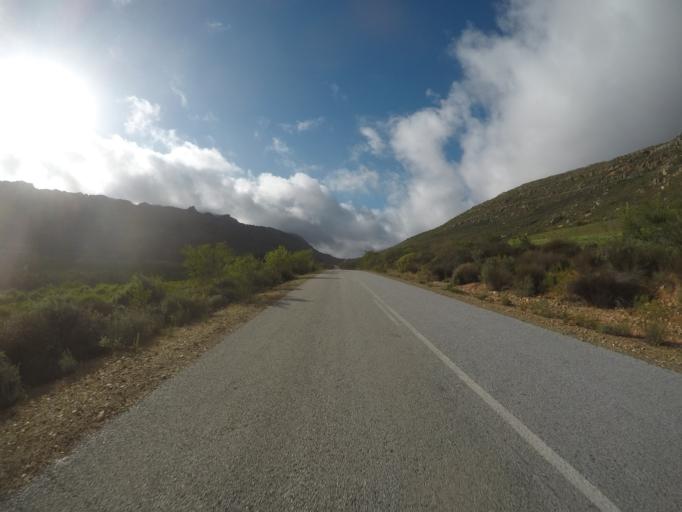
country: ZA
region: Western Cape
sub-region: West Coast District Municipality
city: Clanwilliam
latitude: -32.3648
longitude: 18.8579
